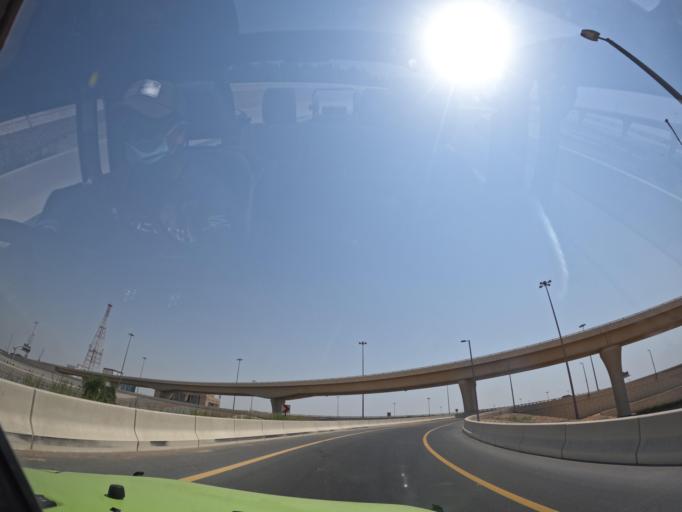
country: AE
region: Abu Dhabi
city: Abu Dhabi
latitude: 24.3114
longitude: 54.6015
